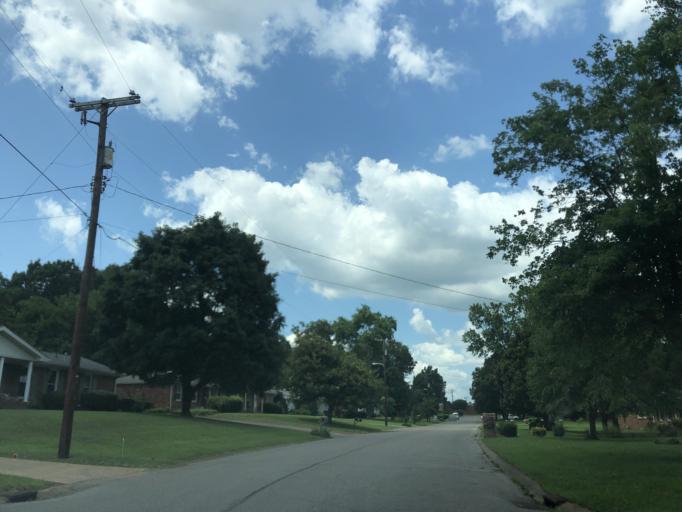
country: US
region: Tennessee
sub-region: Davidson County
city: Lakewood
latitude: 36.2112
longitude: -86.6006
